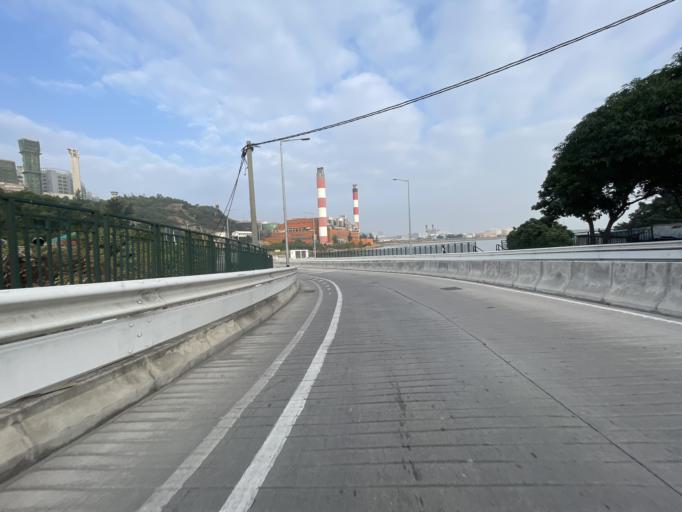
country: MO
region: Macau
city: Macau
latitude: 22.1345
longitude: 113.5815
